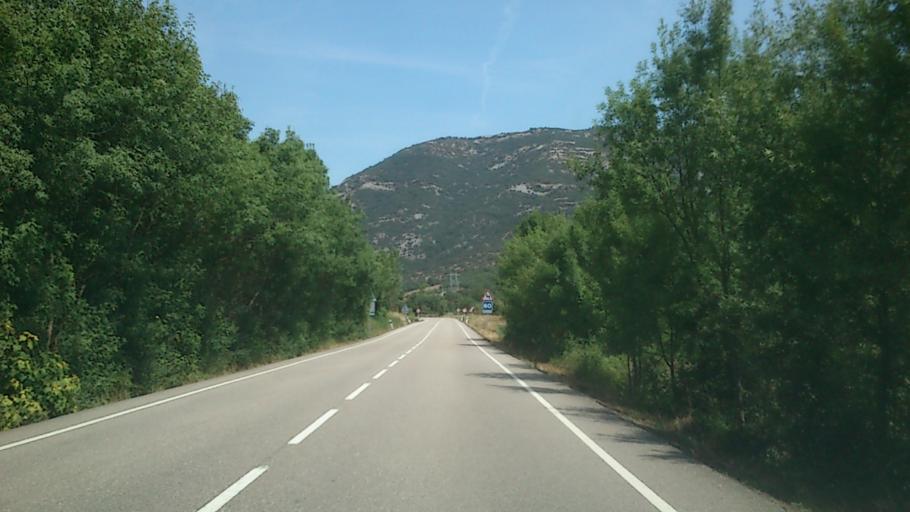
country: ES
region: Castille and Leon
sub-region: Provincia de Burgos
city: Trespaderne
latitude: 42.8775
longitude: -3.3283
